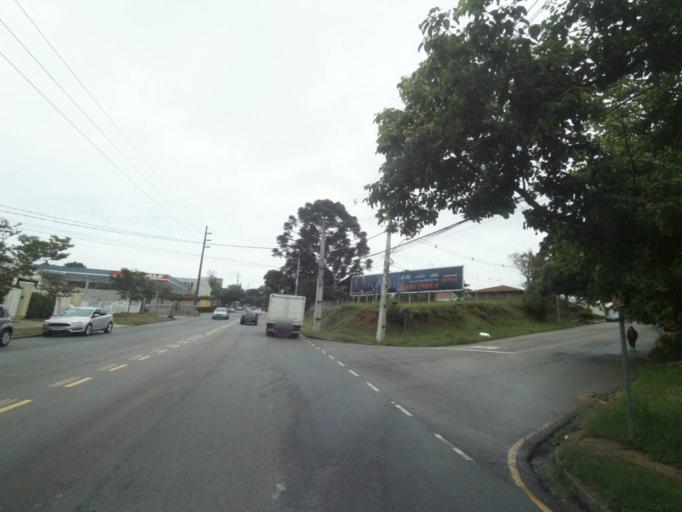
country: BR
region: Parana
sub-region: Curitiba
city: Curitiba
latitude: -25.4062
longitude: -49.2827
